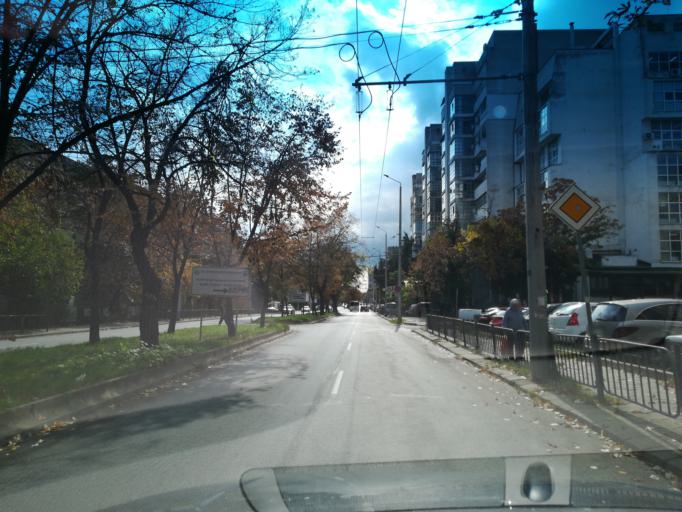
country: BG
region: Stara Zagora
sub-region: Obshtina Stara Zagora
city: Stara Zagora
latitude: 42.4347
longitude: 25.6317
